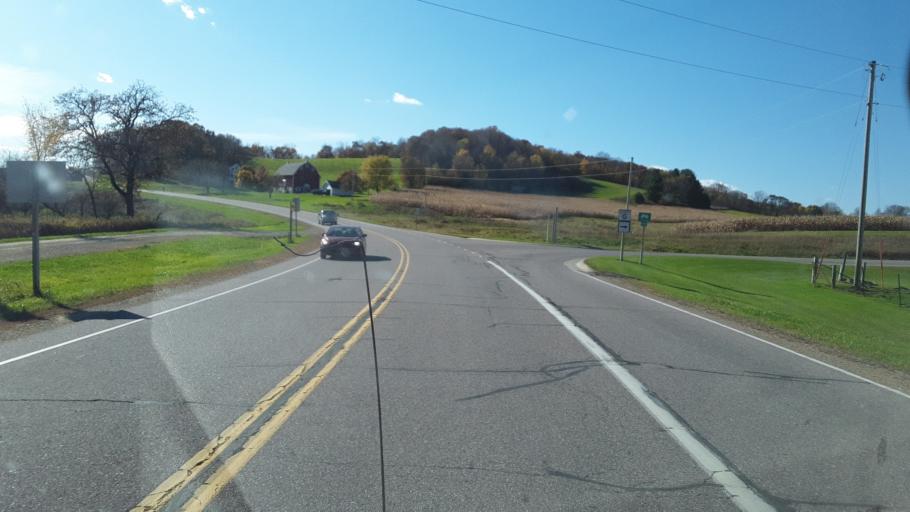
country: US
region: Wisconsin
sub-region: Sauk County
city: Reedsburg
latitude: 43.5407
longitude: -90.1720
